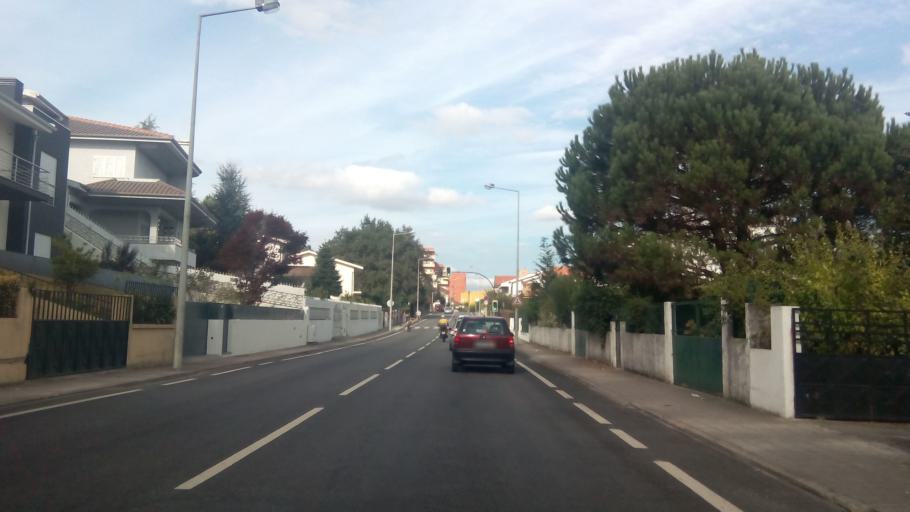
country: PT
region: Porto
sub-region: Paredes
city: Casteloes de Cepeda
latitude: 41.2071
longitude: -8.3410
